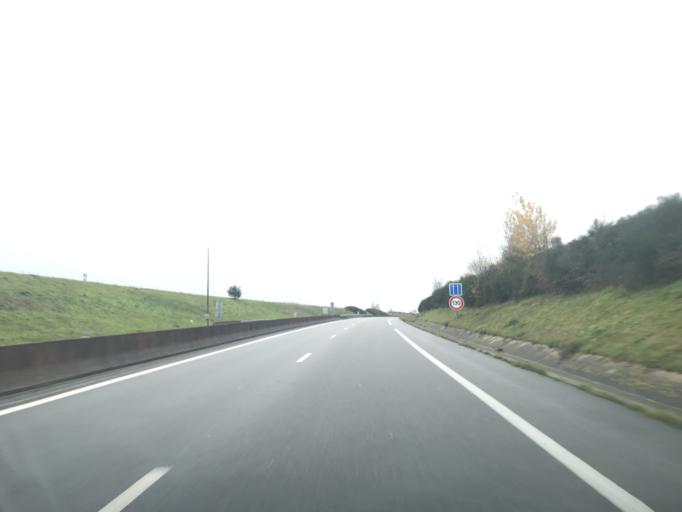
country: FR
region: Haute-Normandie
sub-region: Departement de l'Eure
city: Brionne
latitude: 49.1960
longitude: 0.7704
